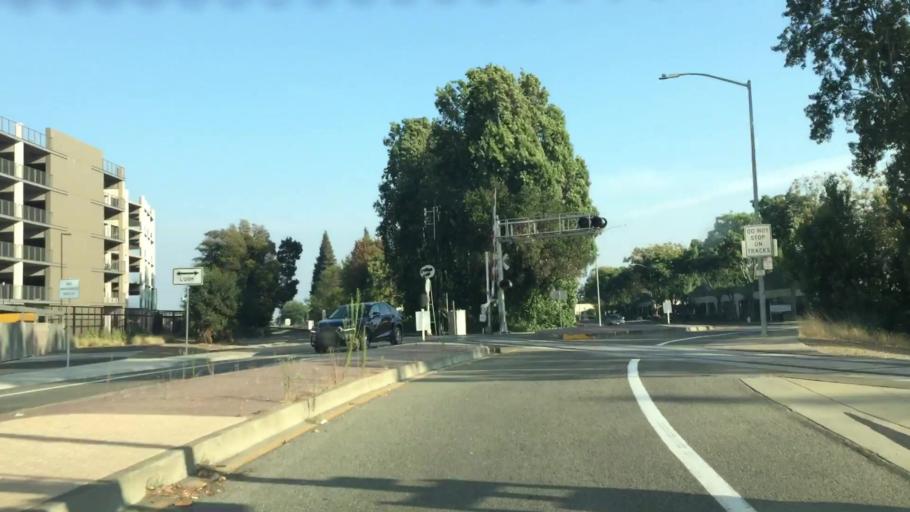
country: US
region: California
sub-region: Alameda County
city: San Leandro
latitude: 37.7208
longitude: -122.1620
